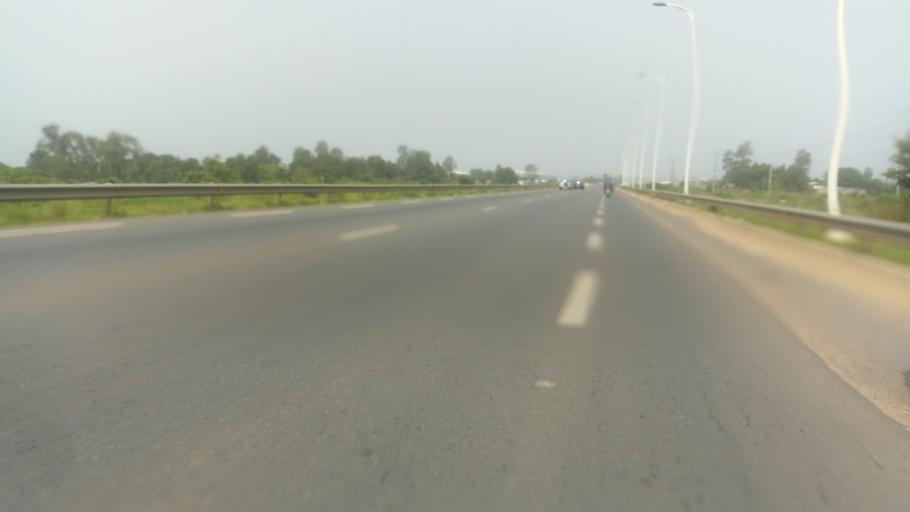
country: TG
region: Maritime
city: Tsevie
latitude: 6.2913
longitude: 1.2132
